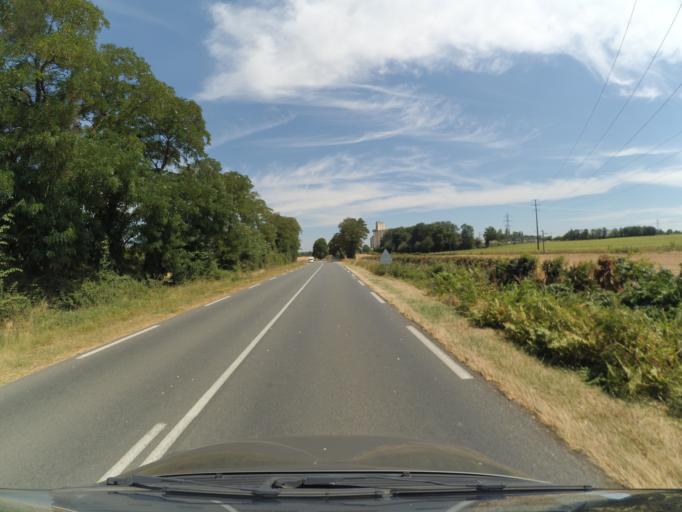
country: FR
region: Poitou-Charentes
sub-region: Departement de la Vienne
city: Lusignan
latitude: 46.4288
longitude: 0.0971
